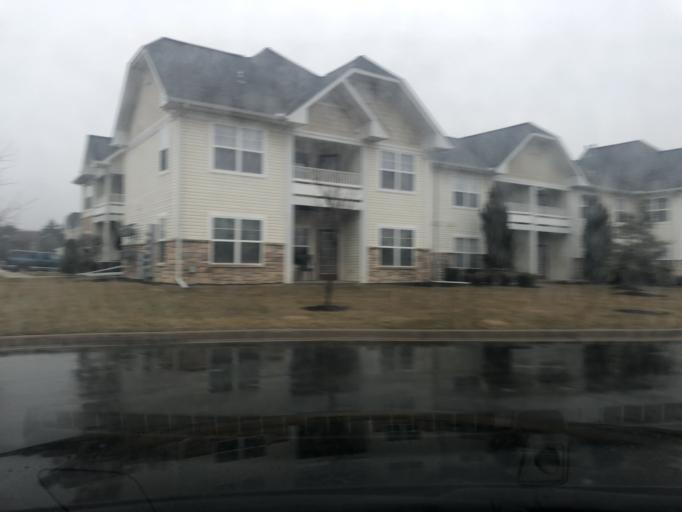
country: US
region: Michigan
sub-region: Wayne County
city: Gibraltar
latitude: 42.1048
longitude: -83.2246
